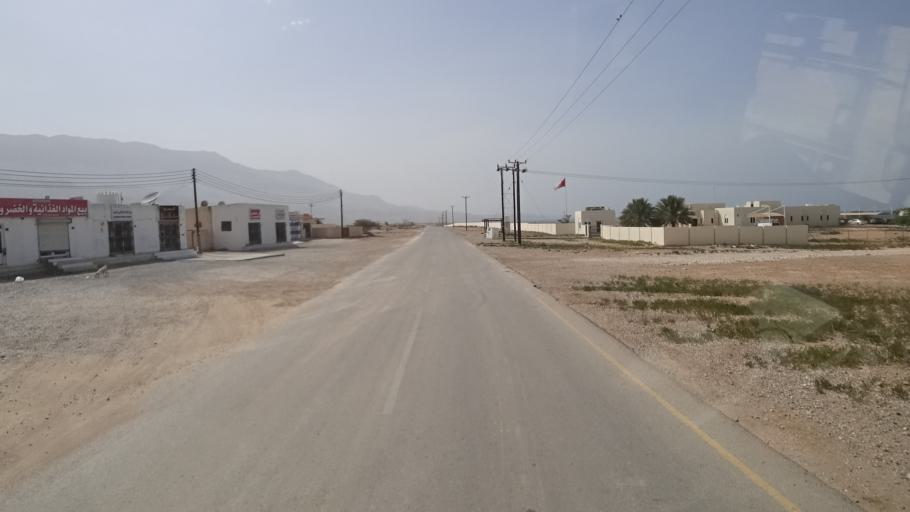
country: OM
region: Ash Sharqiyah
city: Sur
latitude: 22.9915
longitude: 59.1360
